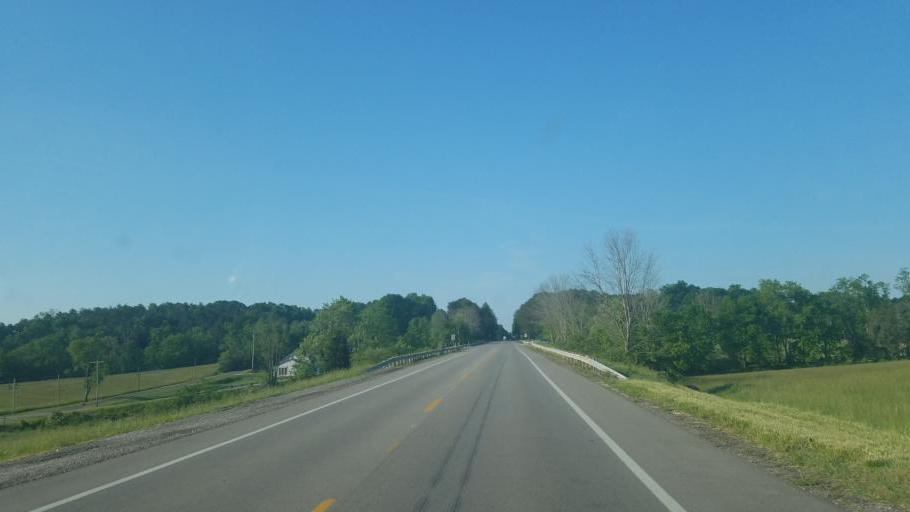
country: US
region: West Virginia
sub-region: Mason County
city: New Haven
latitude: 39.1482
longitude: -81.8527
